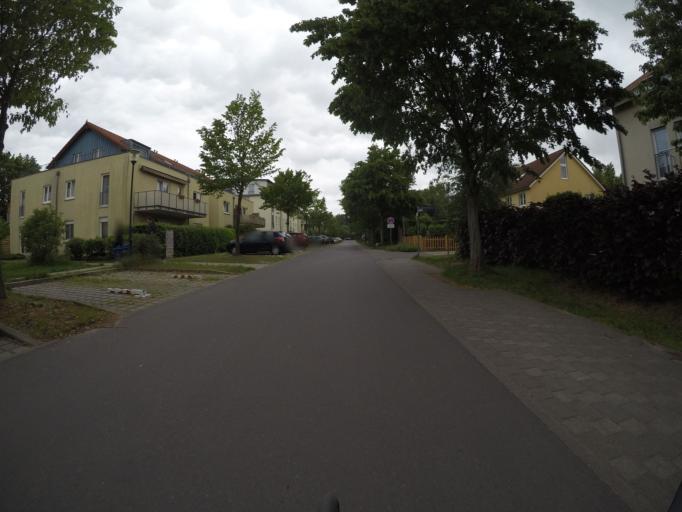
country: DE
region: Brandenburg
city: Glienicke
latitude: 52.6364
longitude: 13.3212
